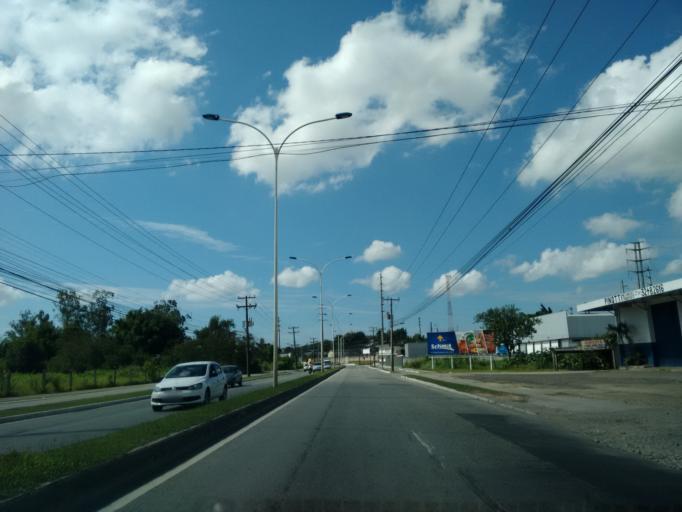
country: BR
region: Santa Catarina
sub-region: Itajai
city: Itajai
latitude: -26.8910
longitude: -48.7177
